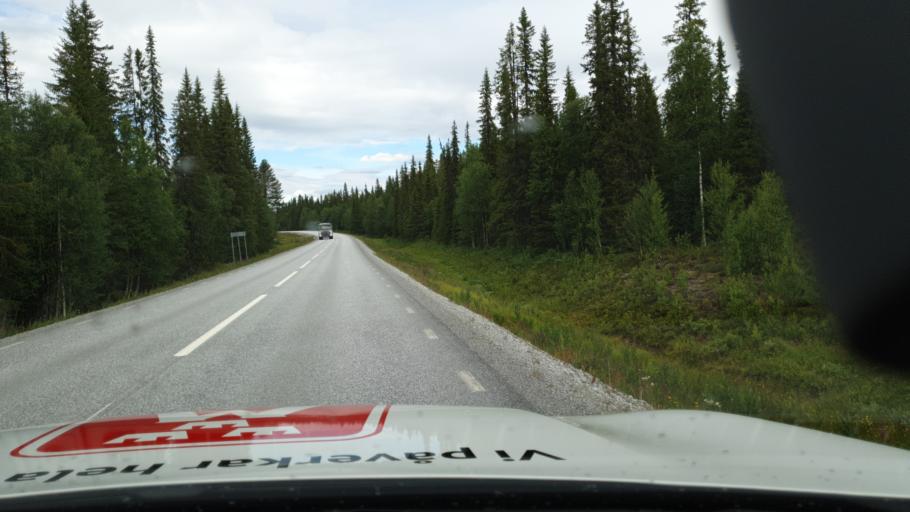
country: SE
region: Vaesterbotten
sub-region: Storumans Kommun
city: Fristad
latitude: 65.2880
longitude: 16.8040
